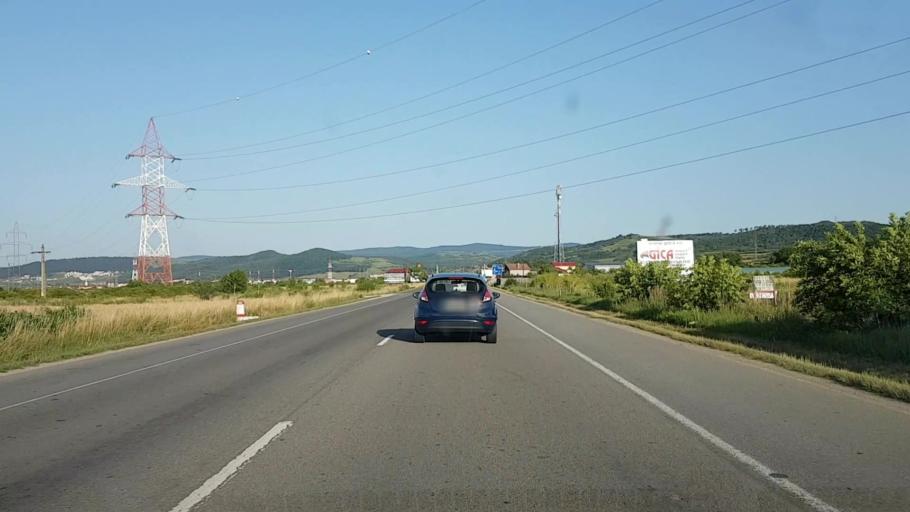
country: RO
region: Cluj
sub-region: Comuna Floresti
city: Luna de Sus
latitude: 46.7487
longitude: 23.4452
